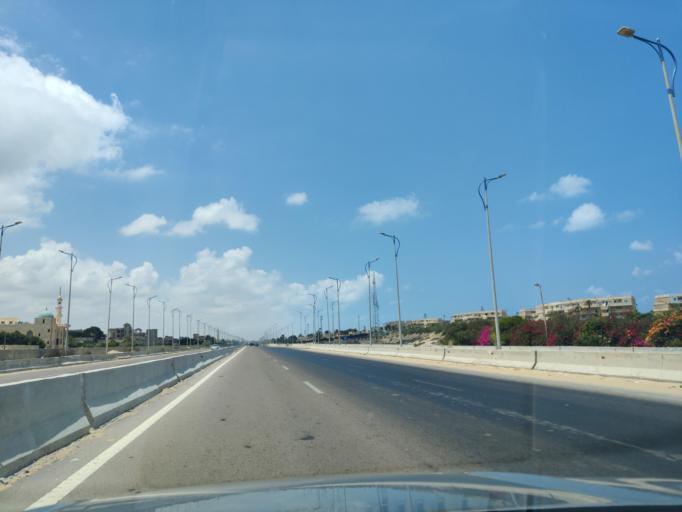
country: EG
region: Muhafazat Matruh
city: Al `Alamayn
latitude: 30.9320
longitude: 29.4817
